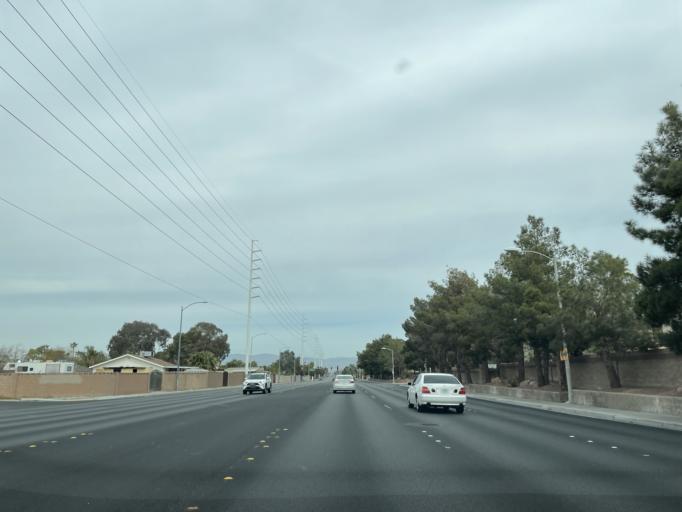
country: US
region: Nevada
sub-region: Clark County
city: Whitney
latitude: 36.0467
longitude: -115.1182
